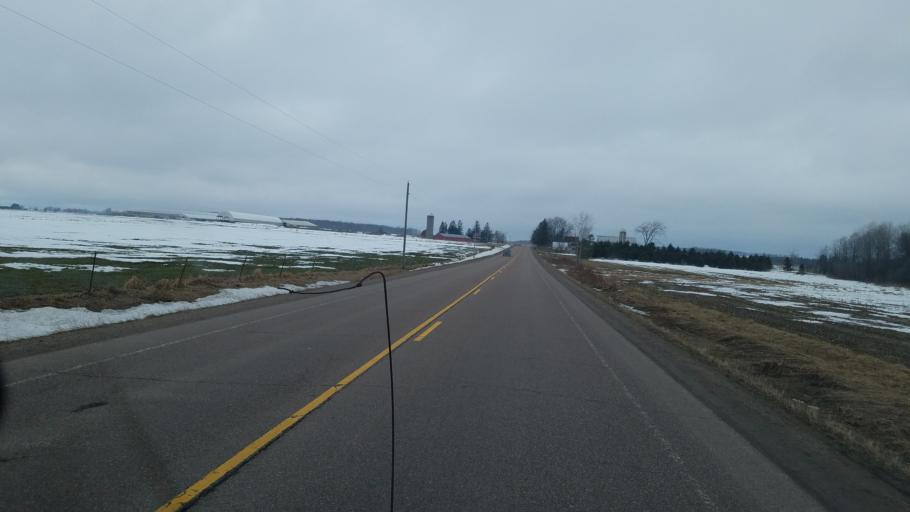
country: US
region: Wisconsin
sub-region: Clark County
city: Loyal
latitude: 44.6546
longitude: -90.4038
